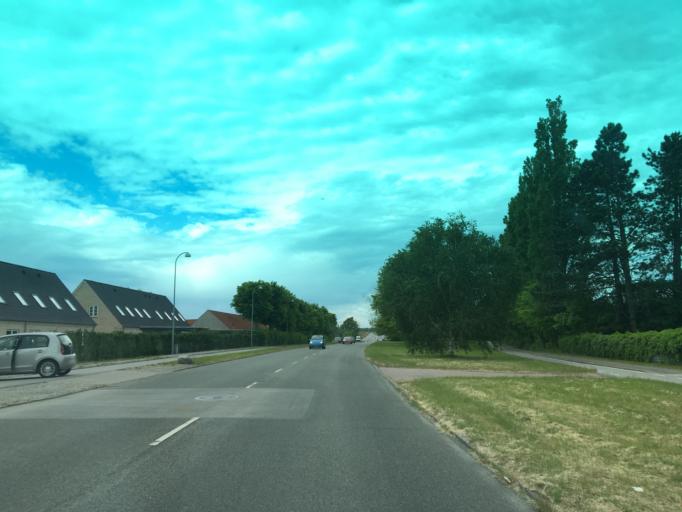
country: DK
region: Capital Region
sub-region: Hvidovre Kommune
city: Hvidovre
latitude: 55.6414
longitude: 12.4462
